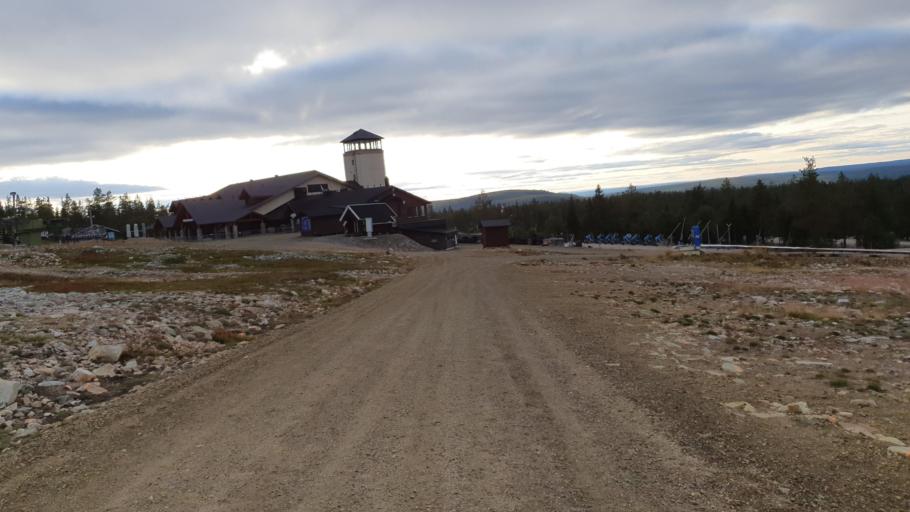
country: FI
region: Lapland
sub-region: Tunturi-Lappi
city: Kolari
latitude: 67.5798
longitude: 24.2065
